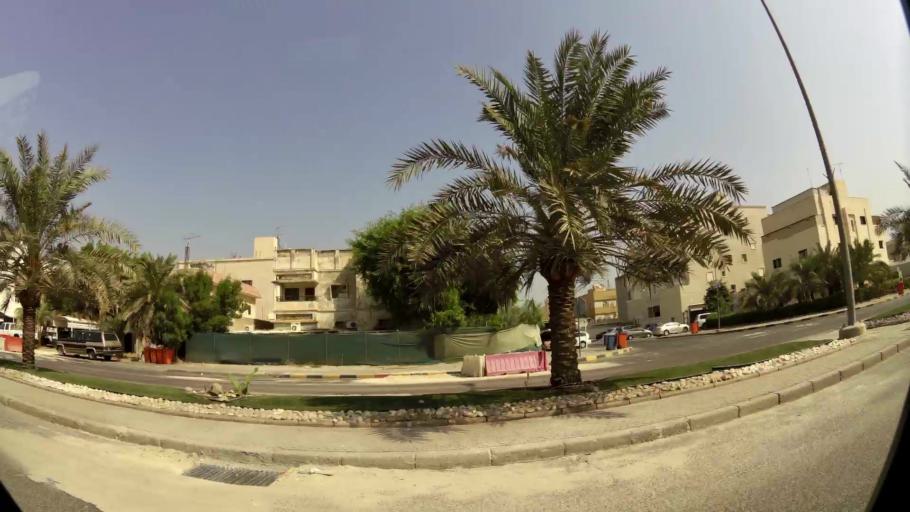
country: KW
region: Al Asimah
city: Ad Dasmah
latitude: 29.3500
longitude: 48.0046
